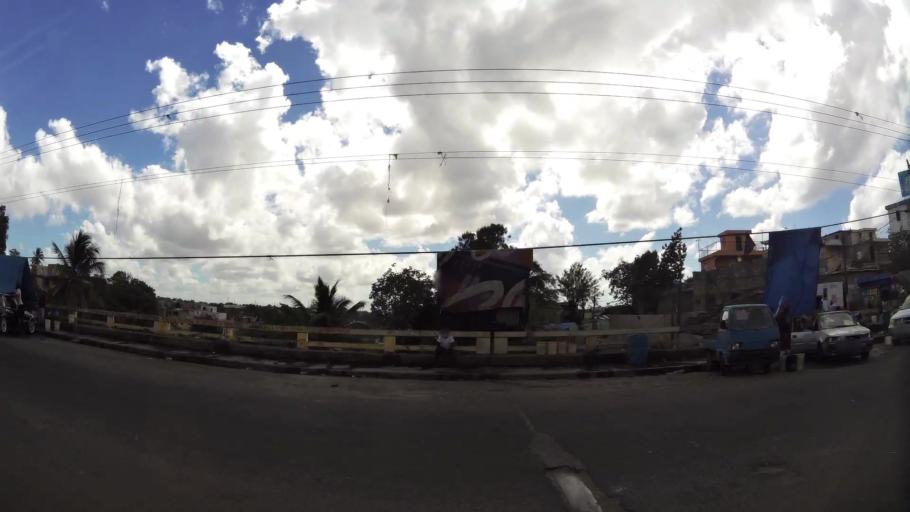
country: DO
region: Nacional
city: Ensanche Luperon
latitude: 18.4993
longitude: -69.8819
